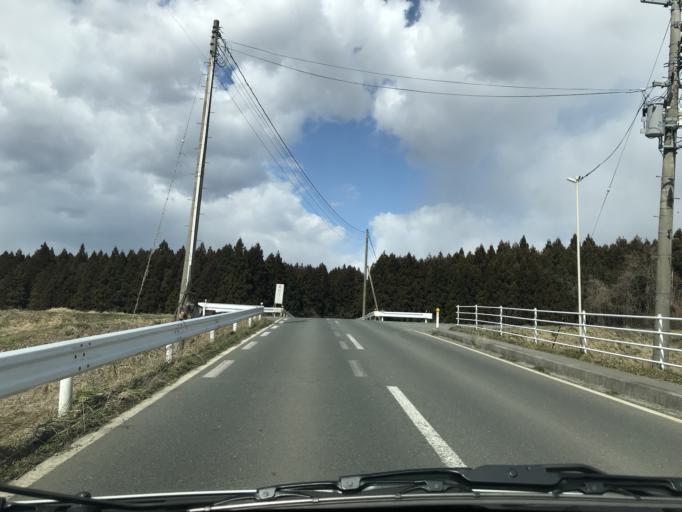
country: JP
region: Iwate
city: Kitakami
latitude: 39.2869
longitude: 141.0677
